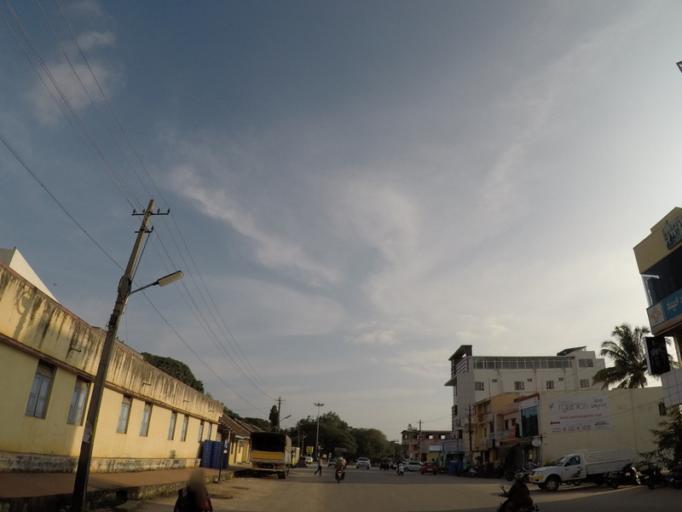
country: IN
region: Karnataka
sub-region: Chikmagalur
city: Chikmagalur
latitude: 13.3144
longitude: 75.7713
